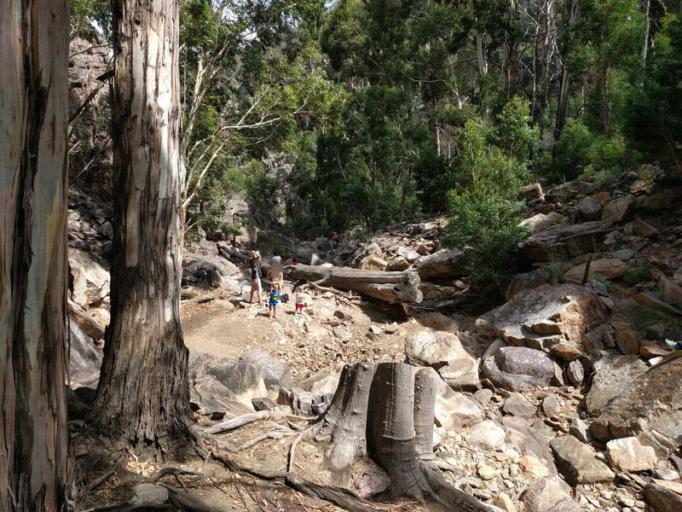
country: AR
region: Buenos Aires
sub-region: Partido de Tornquist
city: Tornquist
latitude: -38.0637
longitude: -62.0163
